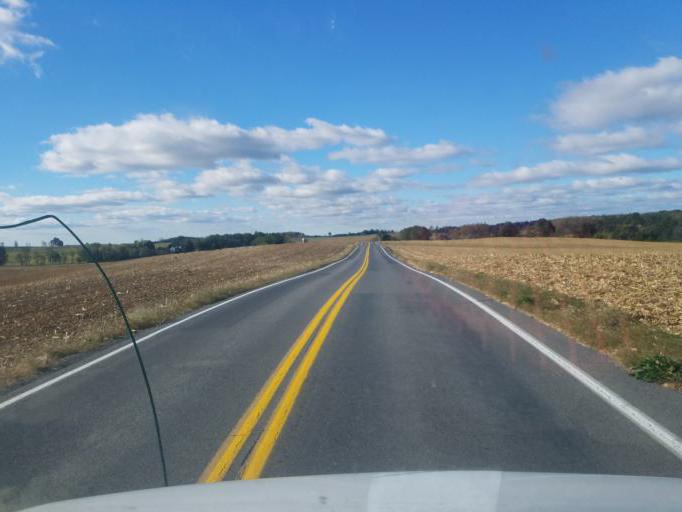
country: US
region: Pennsylvania
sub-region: Franklin County
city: Guilford Siding
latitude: 39.8518
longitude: -77.6061
